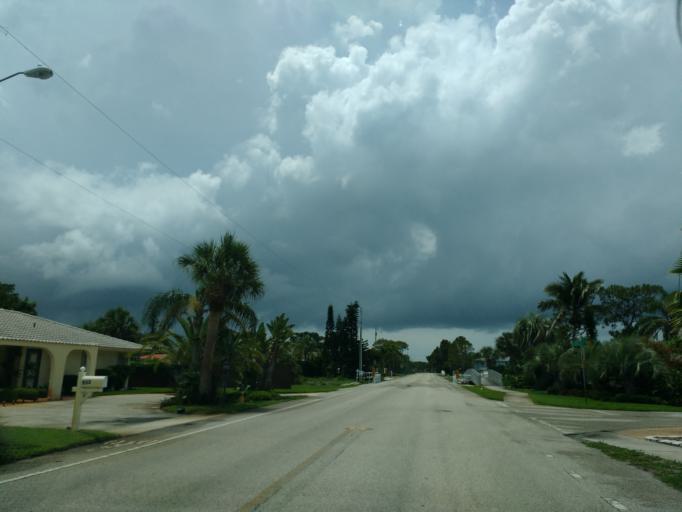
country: US
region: Florida
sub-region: Sarasota County
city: Venice
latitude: 27.0827
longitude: -82.4502
